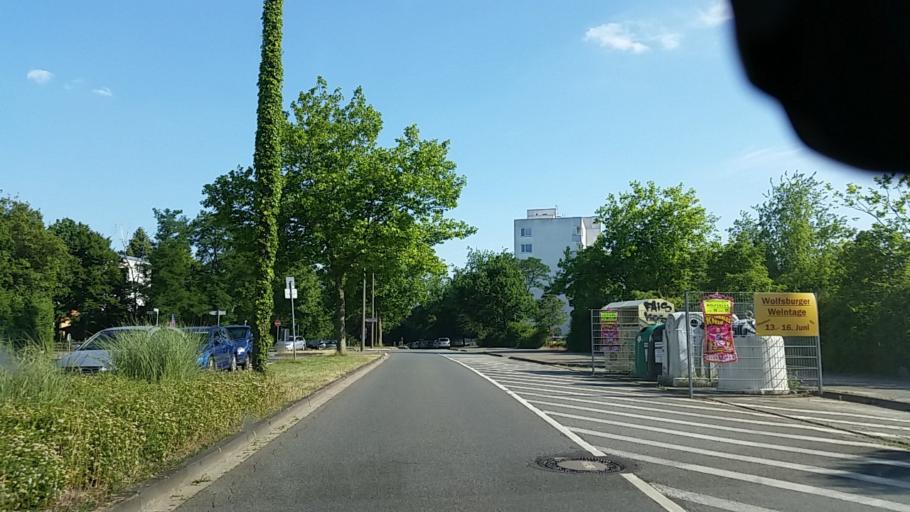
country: DE
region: Lower Saxony
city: Wolfsburg
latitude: 52.4026
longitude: 10.7353
